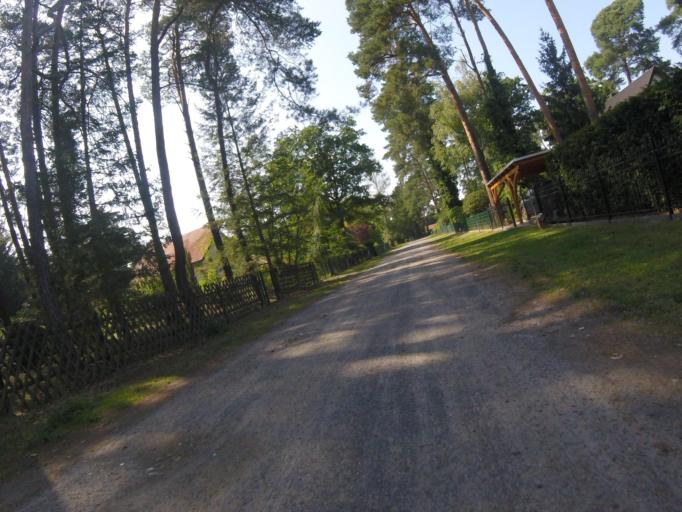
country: DE
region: Brandenburg
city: Bestensee
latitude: 52.2664
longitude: 13.7440
